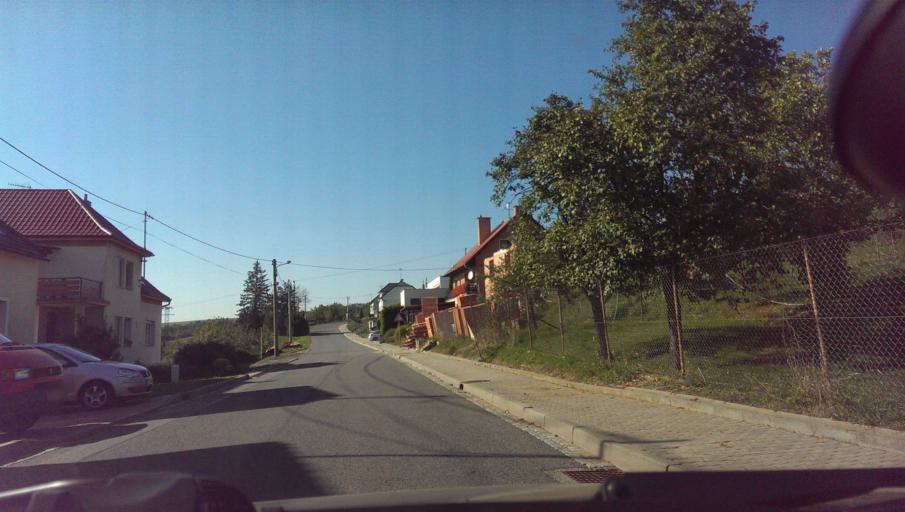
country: CZ
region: Zlin
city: Popovice
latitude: 49.0483
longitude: 17.5238
